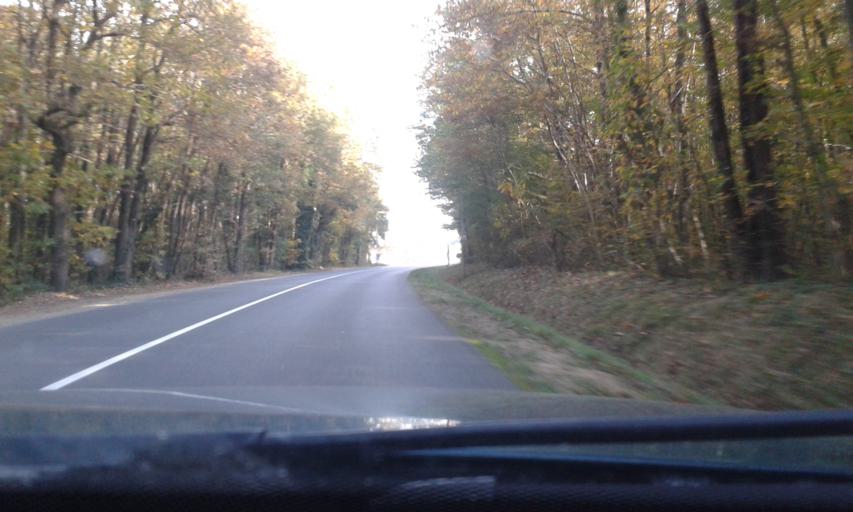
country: FR
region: Centre
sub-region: Departement du Loiret
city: Olivet
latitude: 47.8373
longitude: 1.8739
